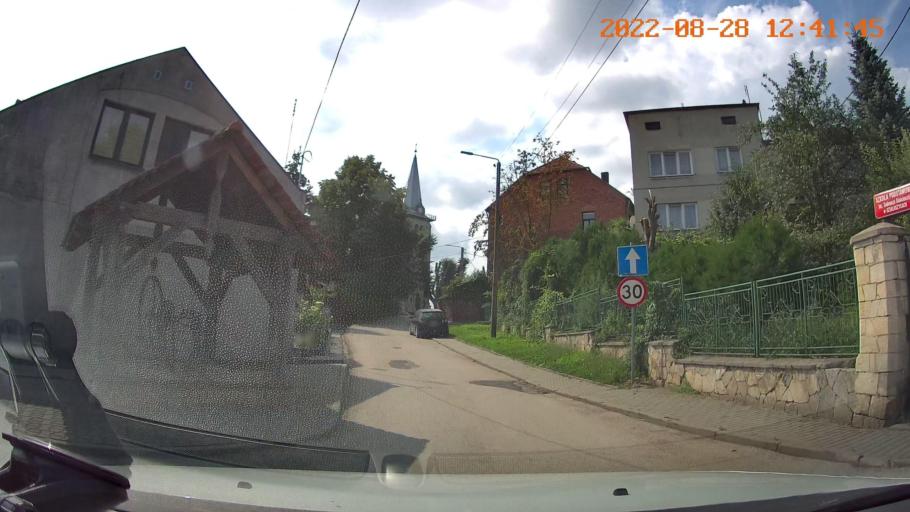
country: PL
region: Swietokrzyskie
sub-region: Powiat pinczowski
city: Dzialoszyce
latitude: 50.3676
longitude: 20.3515
